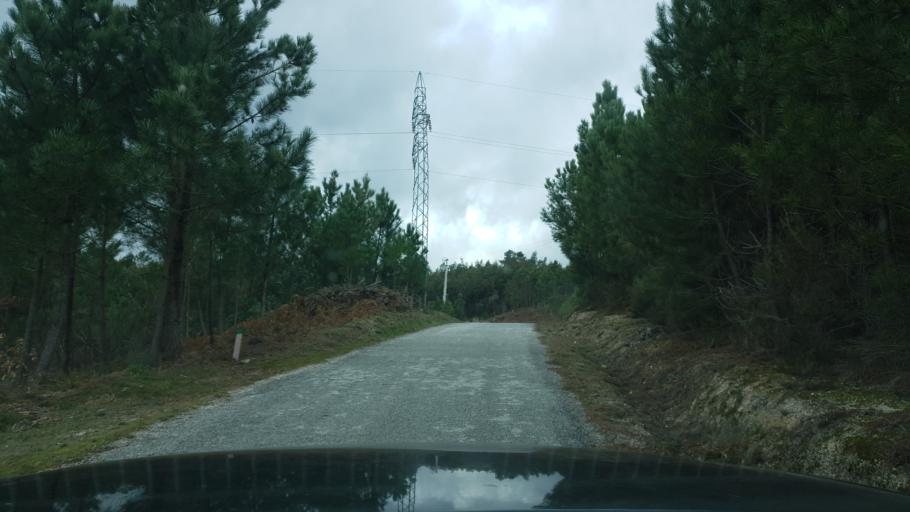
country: PT
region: Viseu
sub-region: Castro Daire
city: Castro Daire
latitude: 40.8730
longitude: -7.9812
